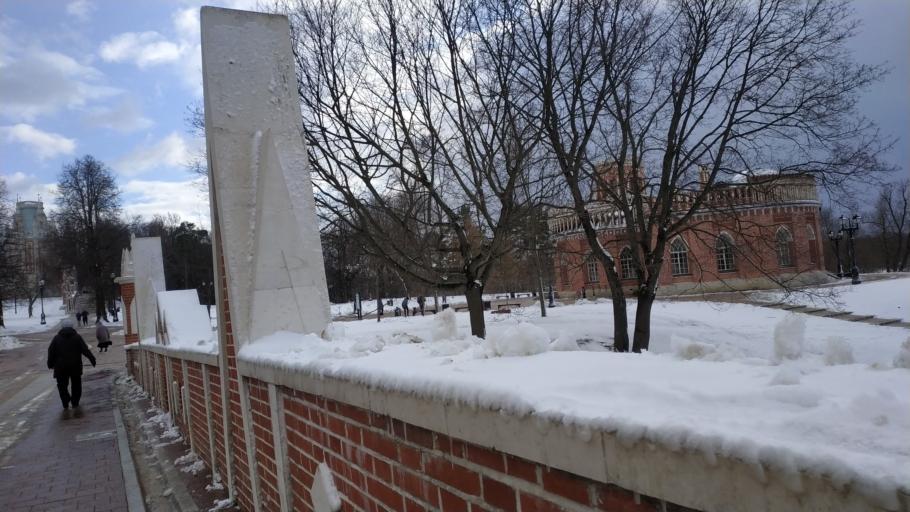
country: RU
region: Moscow
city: Orekhovo-Borisovo Severnoye
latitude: 55.6178
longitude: 37.6806
